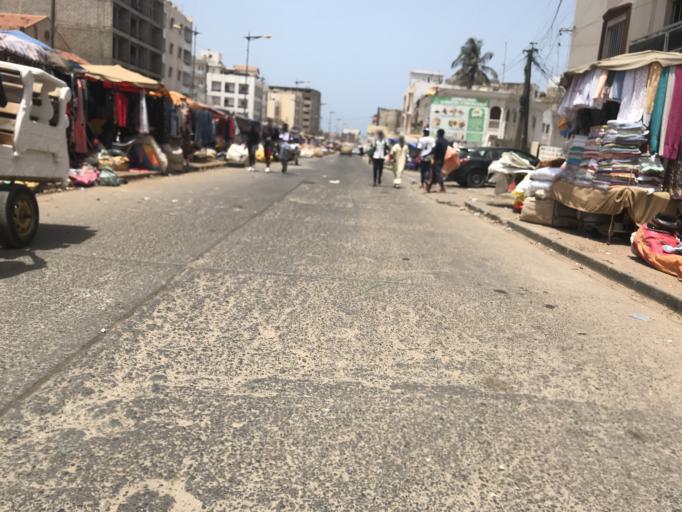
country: SN
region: Dakar
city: Dakar
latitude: 14.6842
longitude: -17.4538
